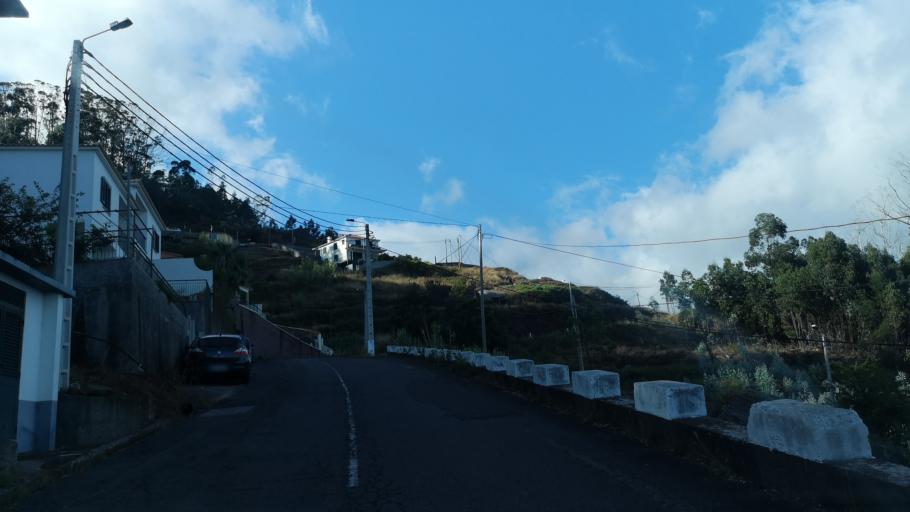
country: PT
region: Madeira
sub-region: Santa Cruz
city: Camacha
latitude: 32.6653
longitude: -16.8372
